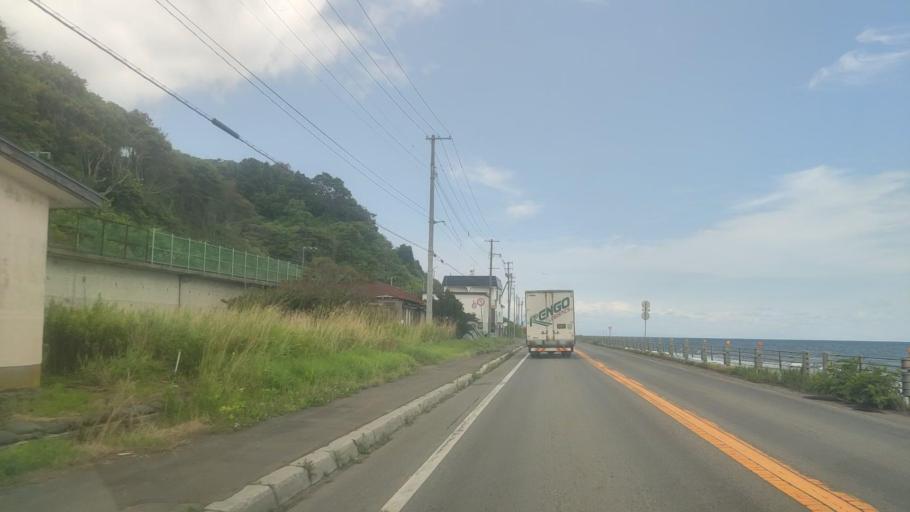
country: JP
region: Hokkaido
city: Nanae
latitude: 42.1440
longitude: 140.5009
